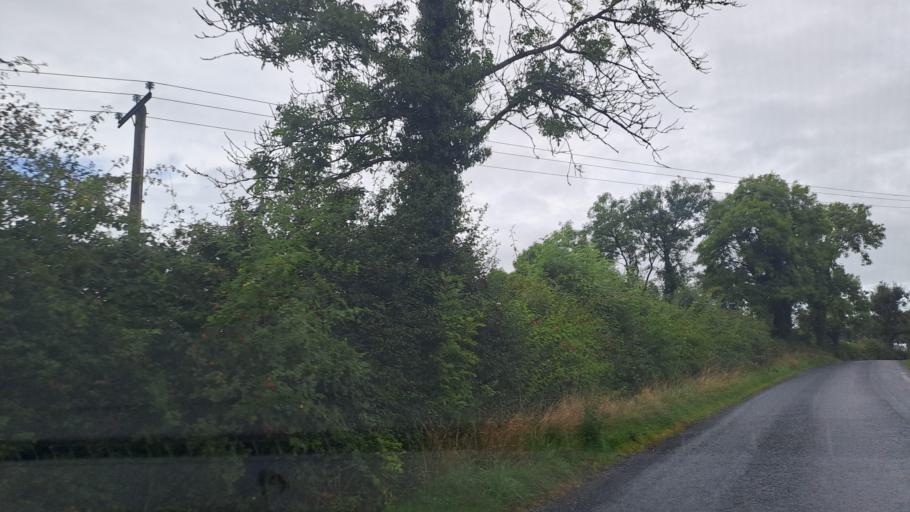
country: IE
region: Ulster
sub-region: County Monaghan
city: Carrickmacross
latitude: 53.9737
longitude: -6.7549
